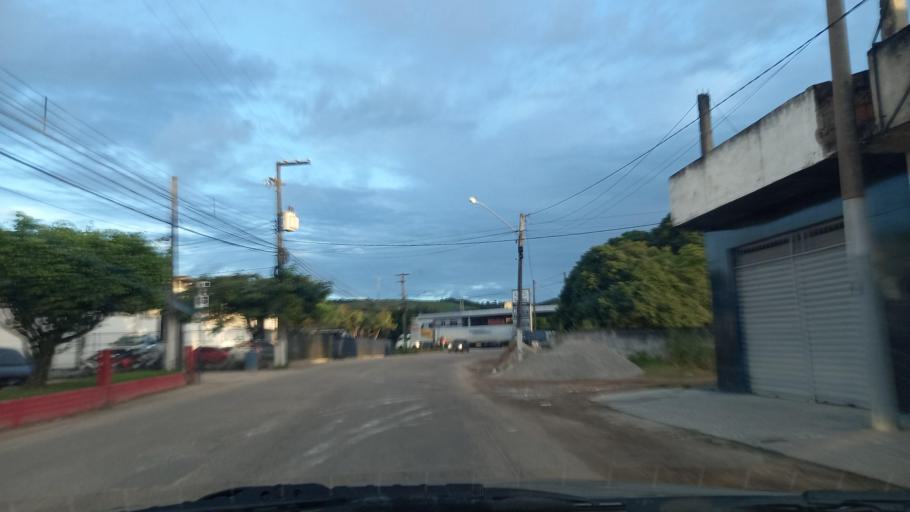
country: BR
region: Pernambuco
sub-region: Palmares
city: Palmares
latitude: -8.6838
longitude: -35.5849
